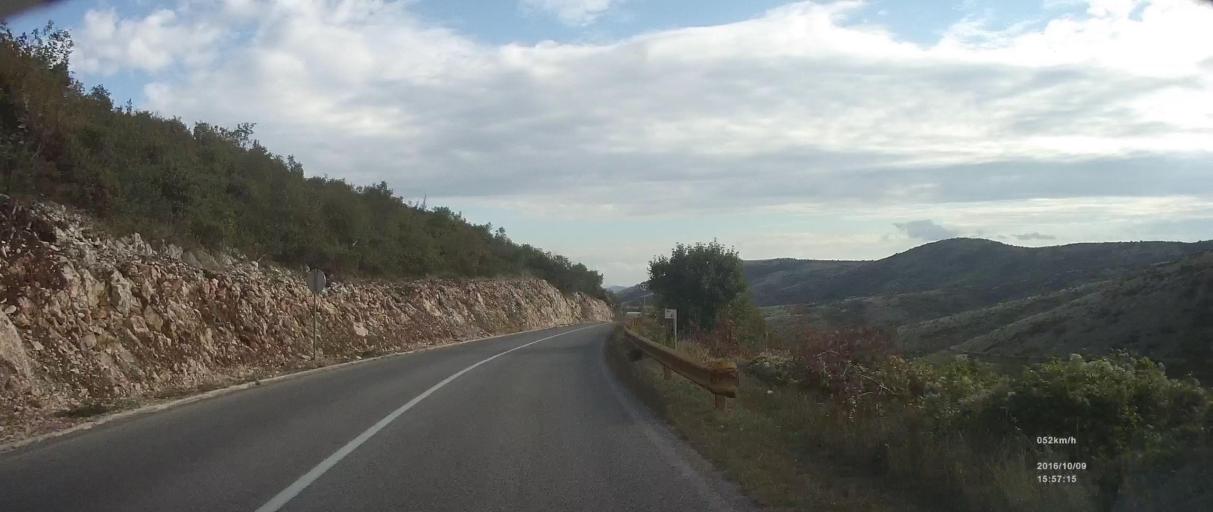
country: HR
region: Splitsko-Dalmatinska
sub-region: Grad Trogir
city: Trogir
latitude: 43.5740
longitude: 16.2373
